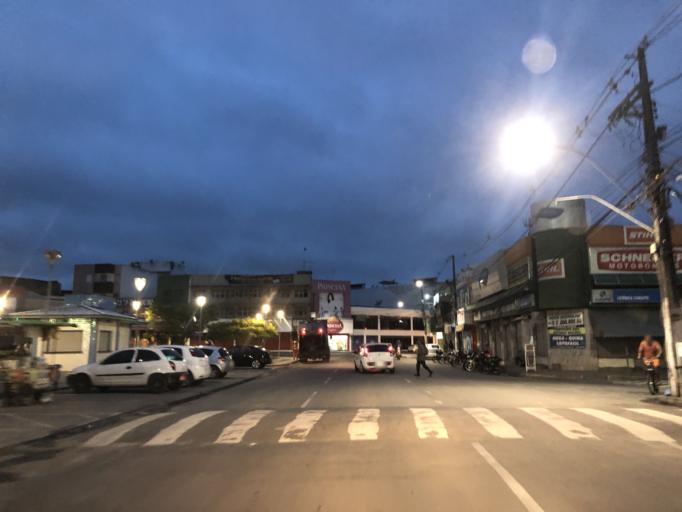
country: BR
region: Bahia
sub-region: Santo Antonio De Jesus
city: Santo Antonio de Jesus
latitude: -12.9689
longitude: -39.2629
